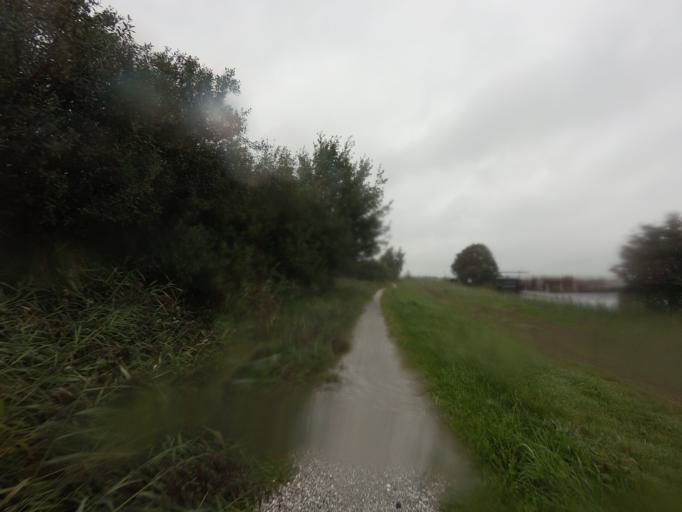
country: NL
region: Friesland
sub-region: Gemeente Smallingerland
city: Oudega
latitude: 53.1010
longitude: 5.9819
